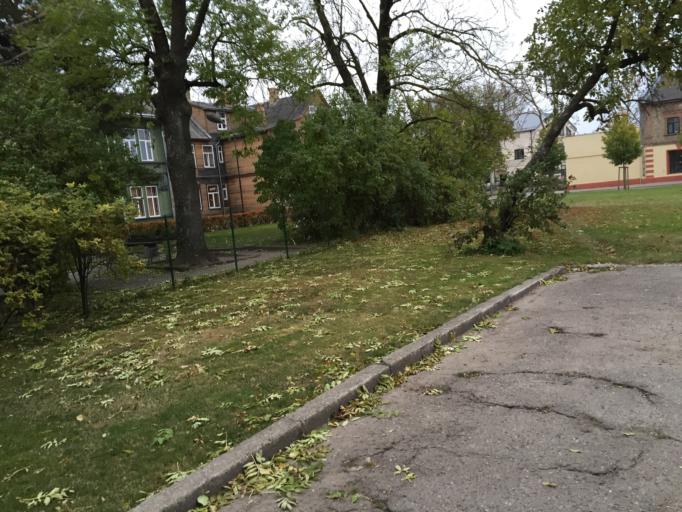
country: LV
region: Jelgava
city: Jelgava
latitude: 56.6460
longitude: 23.7119
